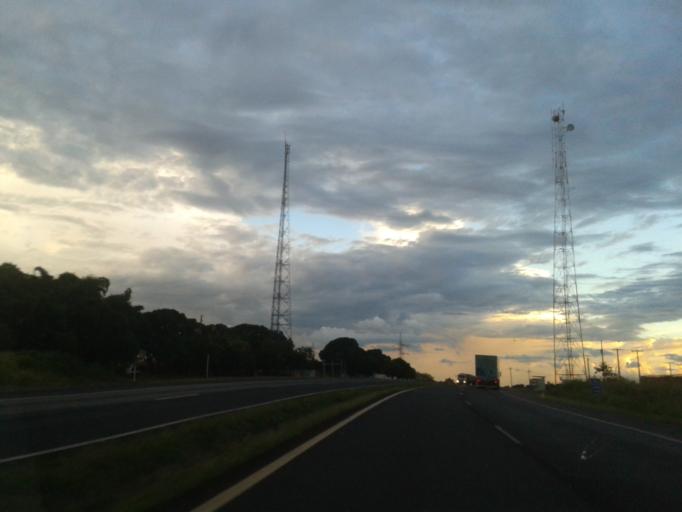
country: BR
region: Minas Gerais
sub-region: Monte Alegre De Minas
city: Monte Alegre de Minas
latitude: -18.7703
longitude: -49.0733
